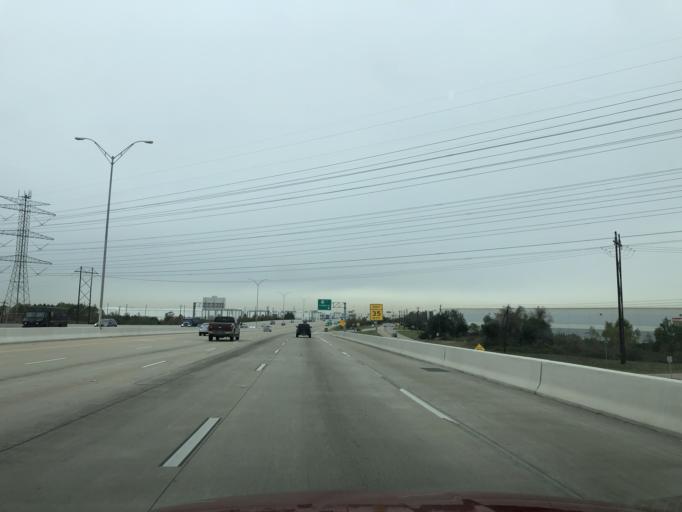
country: US
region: Texas
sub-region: Fort Bend County
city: Missouri City
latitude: 29.6212
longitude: -95.5093
